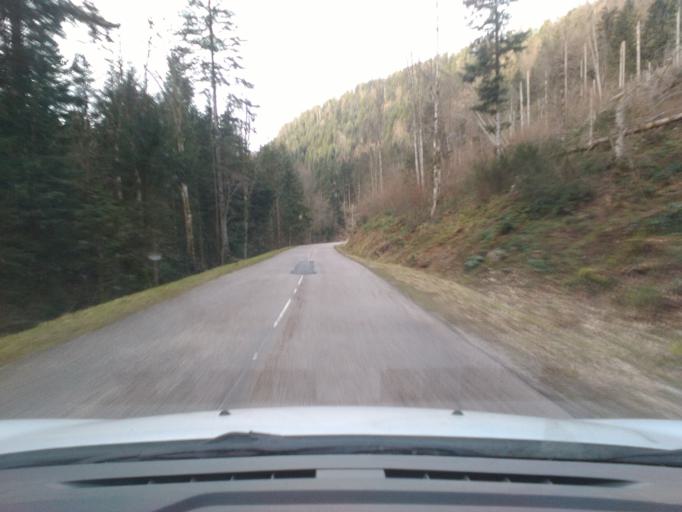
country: FR
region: Lorraine
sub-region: Departement des Vosges
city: Xonrupt-Longemer
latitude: 48.1111
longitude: 6.9672
